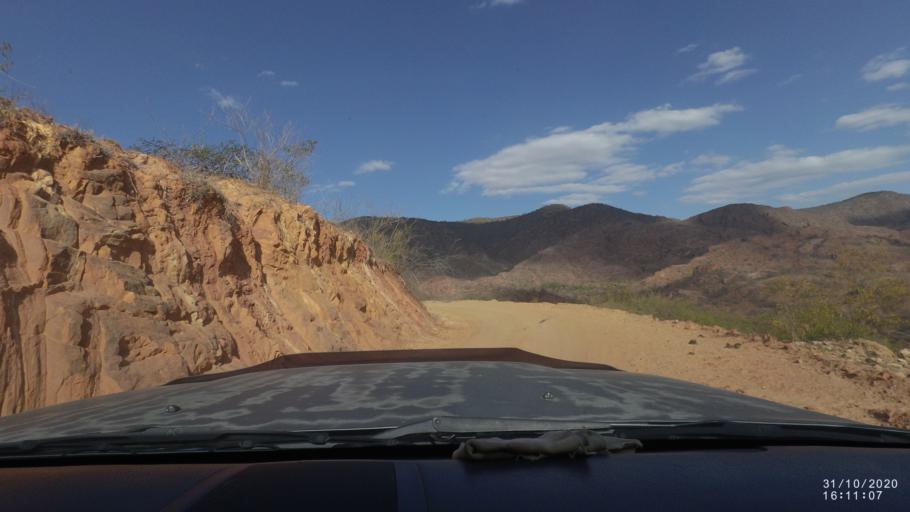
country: BO
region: Chuquisaca
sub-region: Provincia Zudanez
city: Mojocoya
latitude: -18.3809
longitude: -64.6257
